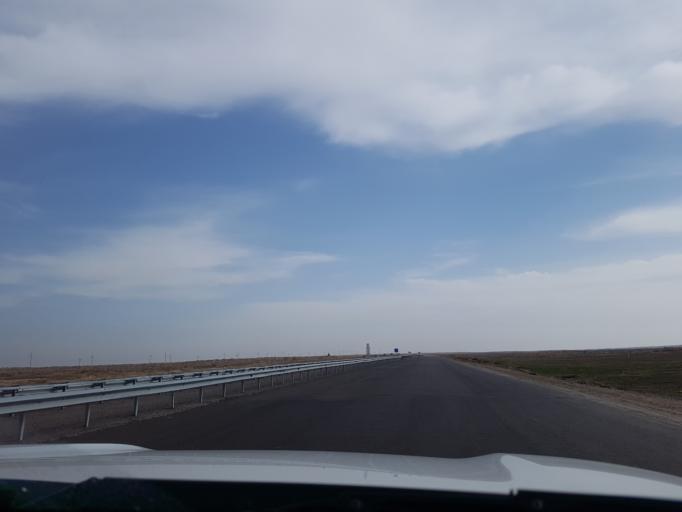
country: TM
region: Mary
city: Mary
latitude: 37.2621
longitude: 61.2688
